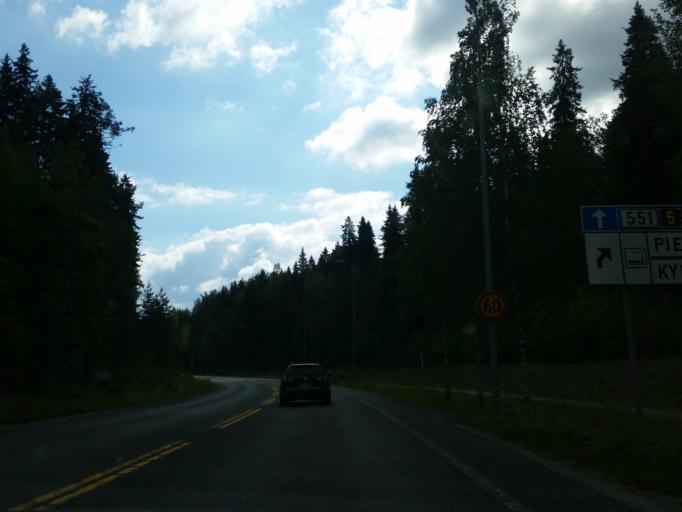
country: FI
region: Northern Savo
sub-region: Kuopio
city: Kuopio
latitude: 62.8399
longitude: 27.5906
